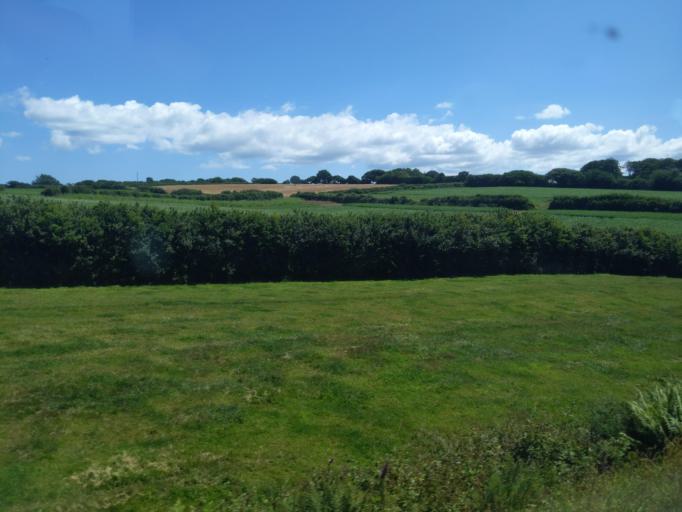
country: GB
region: England
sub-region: Cornwall
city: Saint Stephen
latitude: 50.3336
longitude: -4.8466
